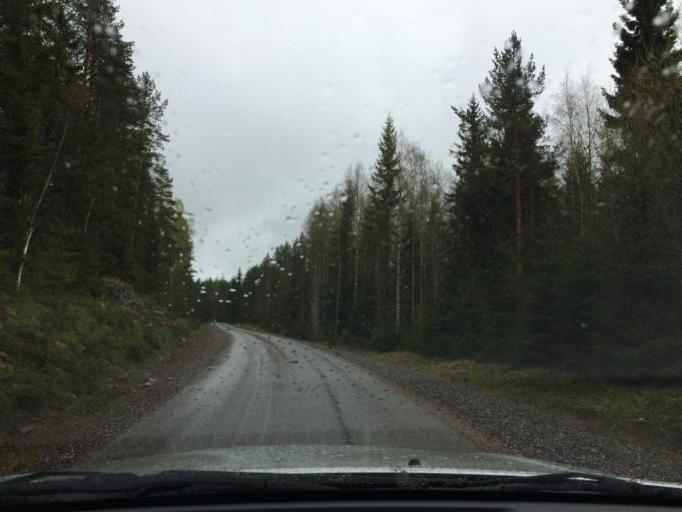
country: SE
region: Dalarna
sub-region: Ludvika Kommun
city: Abborrberget
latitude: 60.0391
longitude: 14.6419
